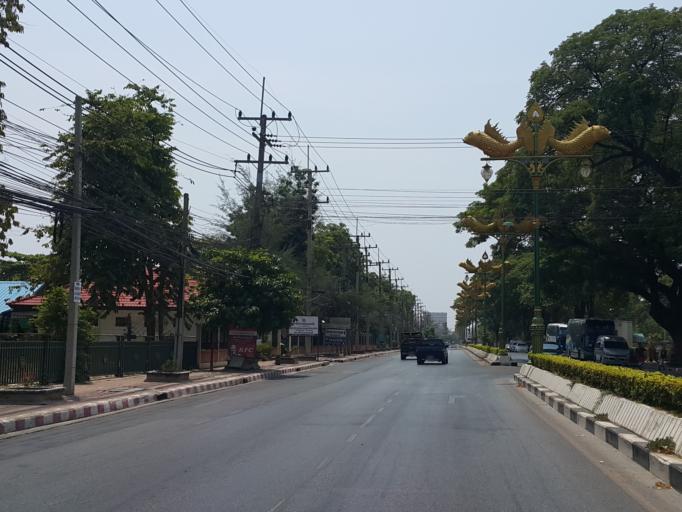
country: TH
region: Kanchanaburi
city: Kanchanaburi
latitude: 14.0330
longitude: 99.5249
